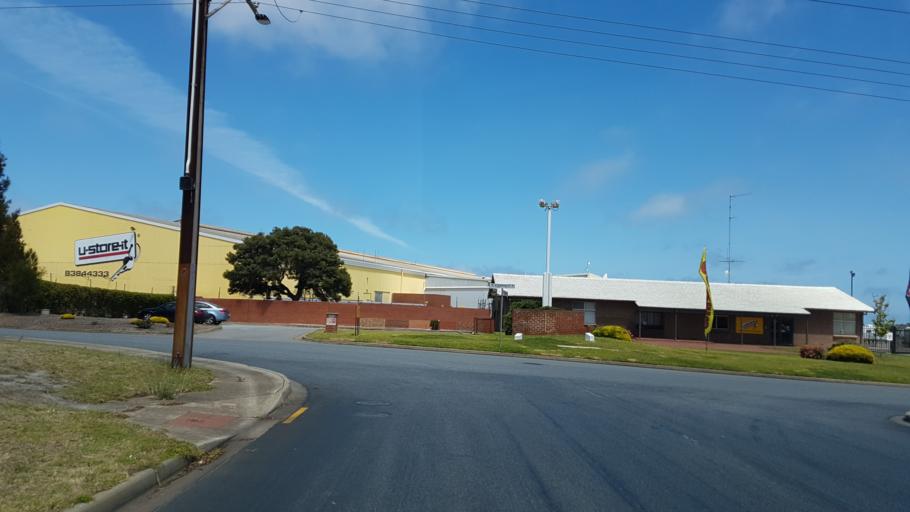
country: AU
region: South Australia
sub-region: Onkaparinga
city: Morphett Vale
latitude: -35.1135
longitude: 138.4973
